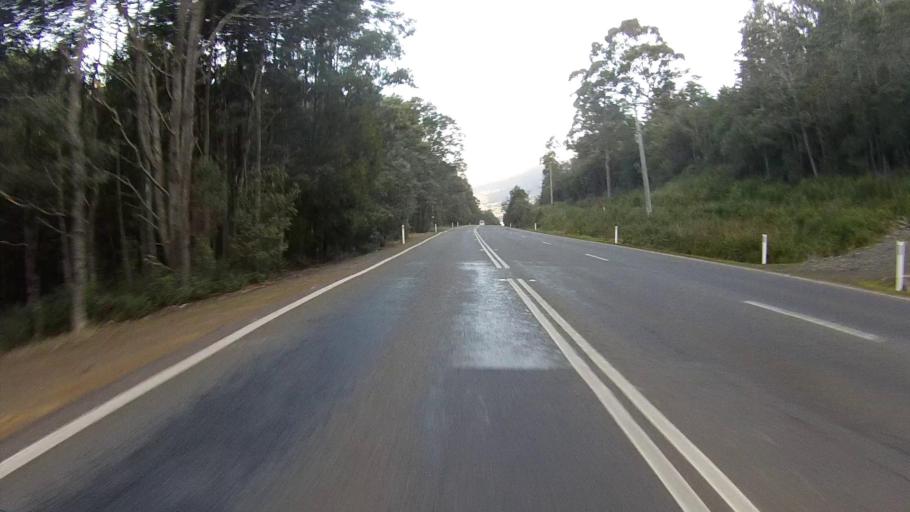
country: AU
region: Tasmania
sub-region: Sorell
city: Sorell
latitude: -42.9990
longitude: 147.9266
